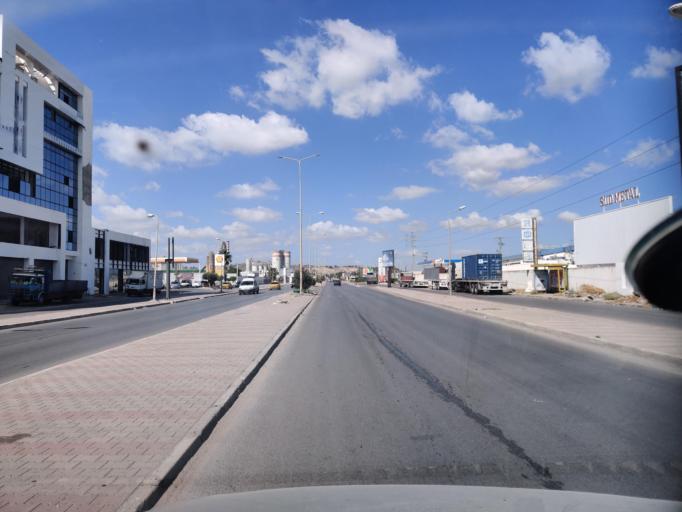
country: TN
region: Bin 'Arus
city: Ben Arous
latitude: 36.7756
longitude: 10.2144
